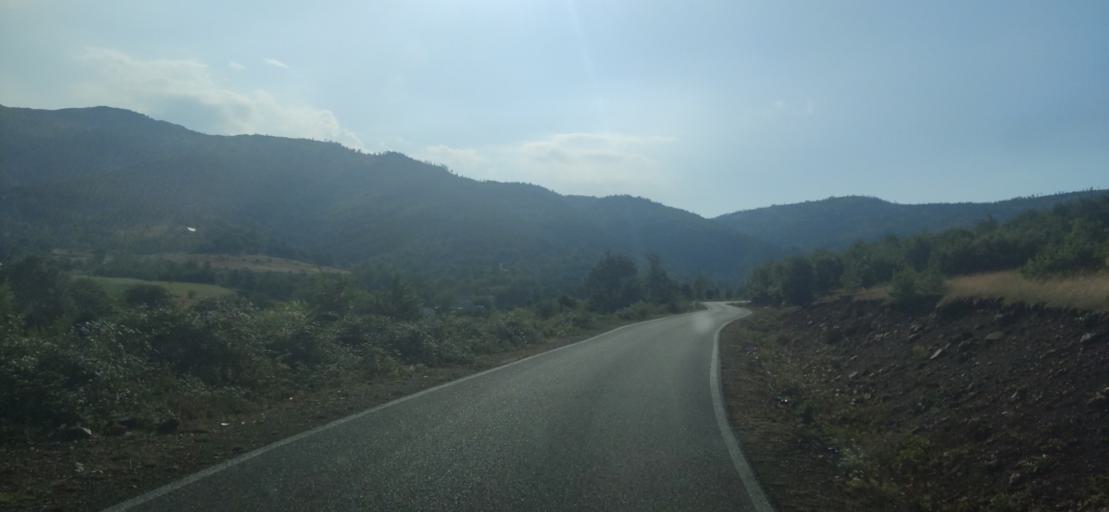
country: AL
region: Shkoder
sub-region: Rrethi i Pukes
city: Iballe
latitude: 42.1823
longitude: 19.9972
